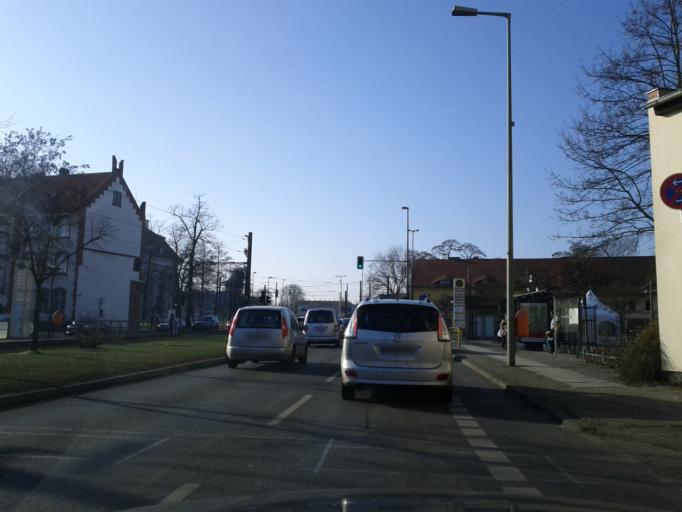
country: DE
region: Berlin
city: Kopenick Bezirk
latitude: 52.4445
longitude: 13.5753
